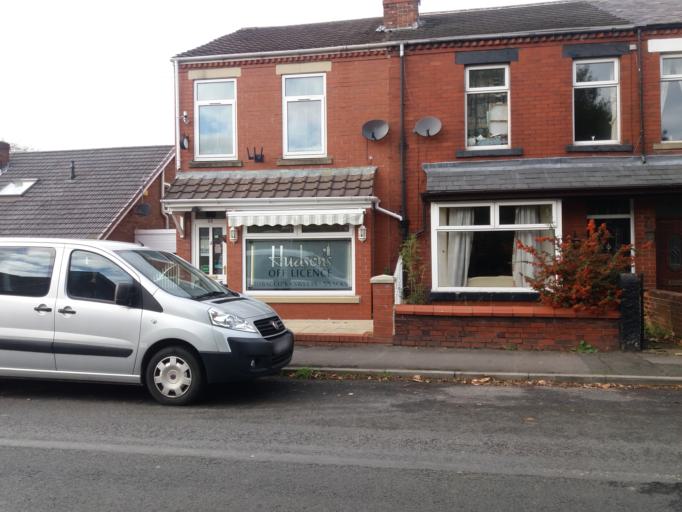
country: GB
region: England
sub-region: Lancashire
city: Coppull
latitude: 53.6247
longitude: -2.6528
